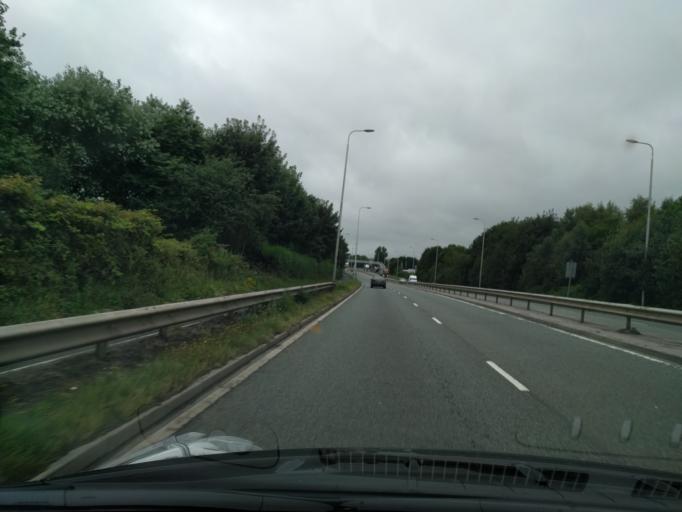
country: GB
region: England
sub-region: Borough of Wigan
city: Ashton in Makerfield
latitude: 53.4722
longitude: -2.6477
